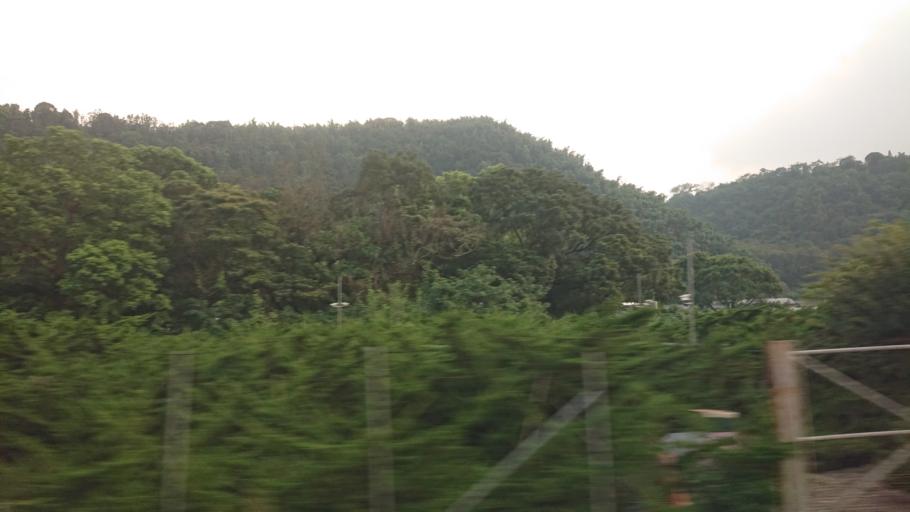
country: TW
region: Taiwan
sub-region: Nantou
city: Puli
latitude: 23.9735
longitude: 120.9932
